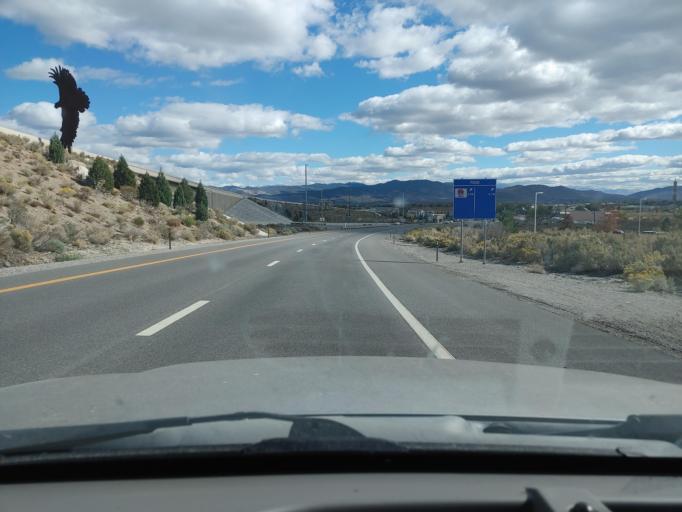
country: US
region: Nevada
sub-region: Carson City
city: Carson City
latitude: 39.2029
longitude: -119.7817
